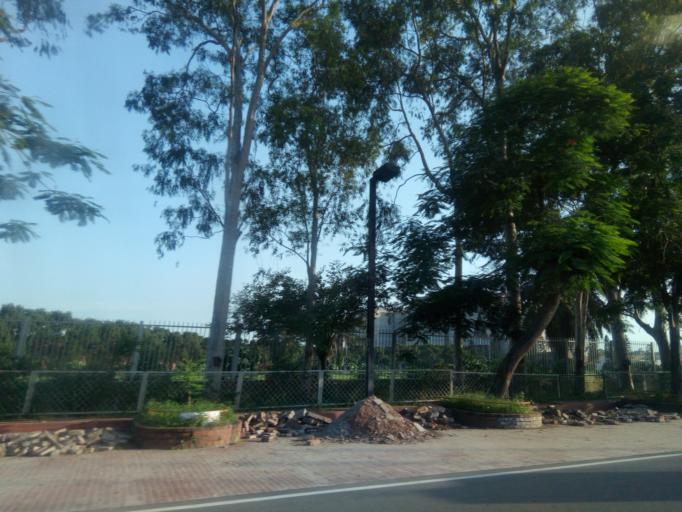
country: BD
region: Dhaka
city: Azimpur
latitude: 23.7648
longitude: 90.3803
